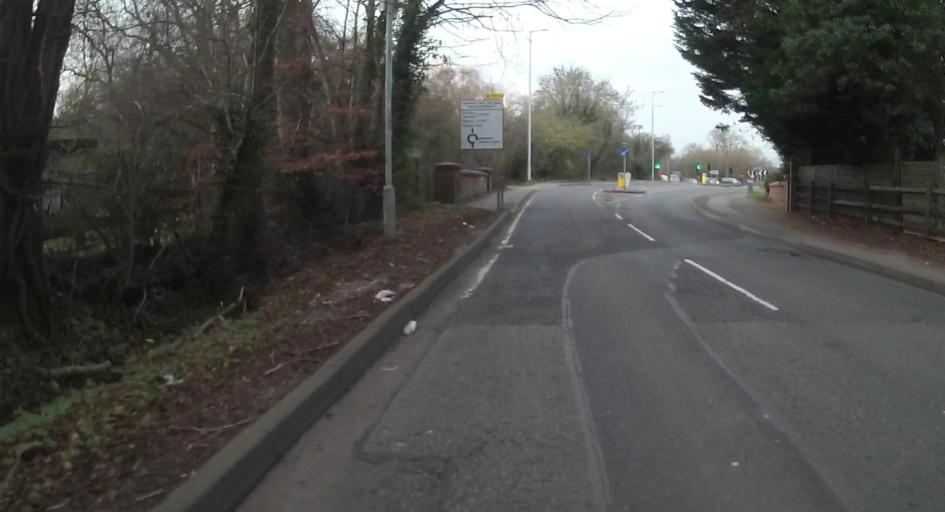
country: GB
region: England
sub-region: Bracknell Forest
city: Bracknell
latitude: 51.4262
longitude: -0.7653
